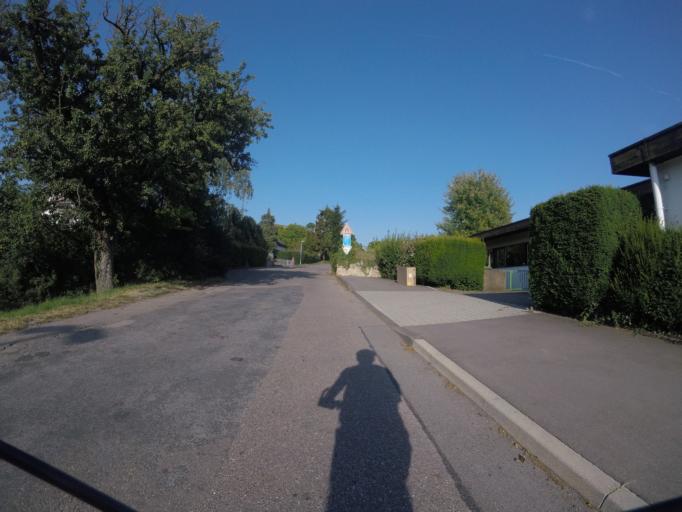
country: DE
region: Baden-Wuerttemberg
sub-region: Regierungsbezirk Stuttgart
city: Asperg
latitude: 48.9095
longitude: 9.1331
